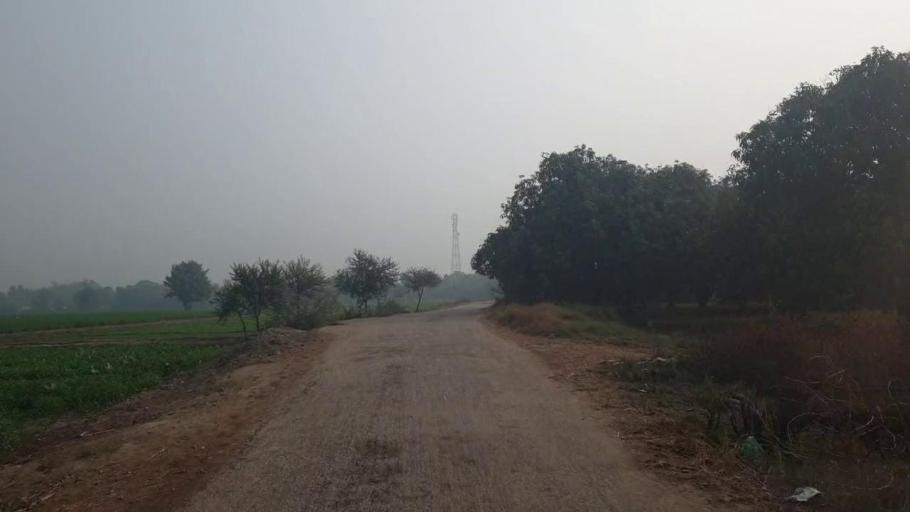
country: PK
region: Sindh
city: Tando Adam
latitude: 25.7238
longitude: 68.6702
